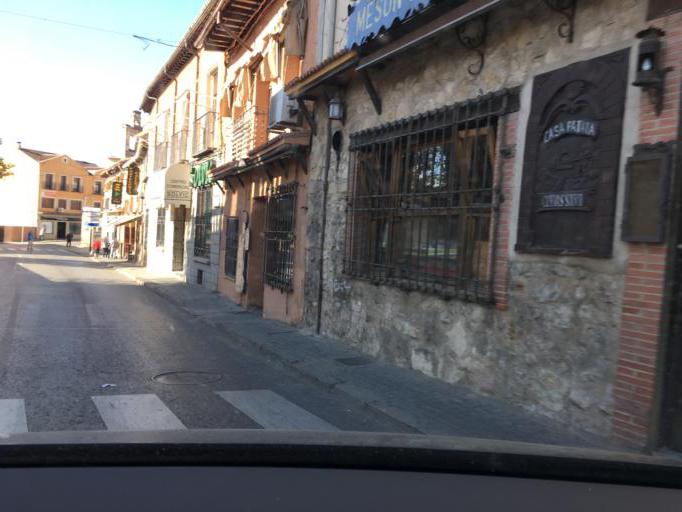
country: ES
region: Madrid
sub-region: Provincia de Madrid
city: Torrelaguna
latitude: 40.8266
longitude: -3.5383
